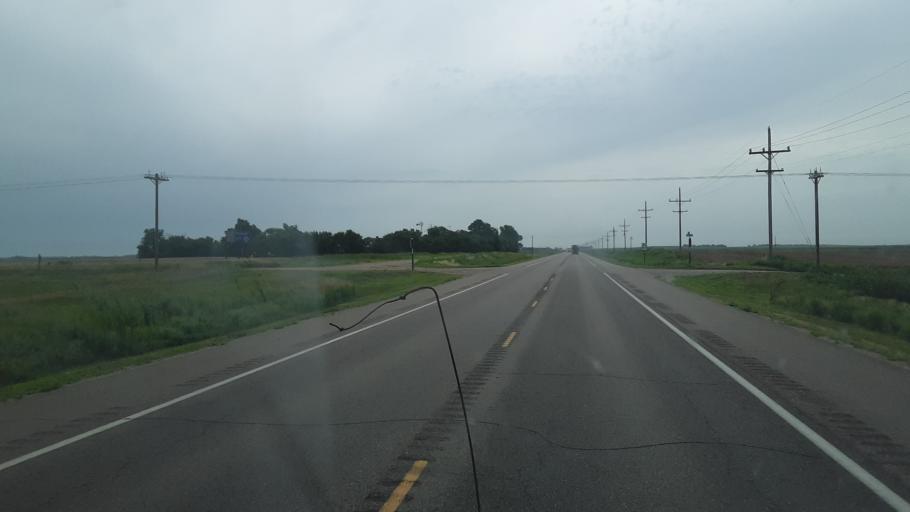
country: US
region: Kansas
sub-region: Edwards County
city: Kinsley
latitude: 37.9274
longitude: -99.3153
